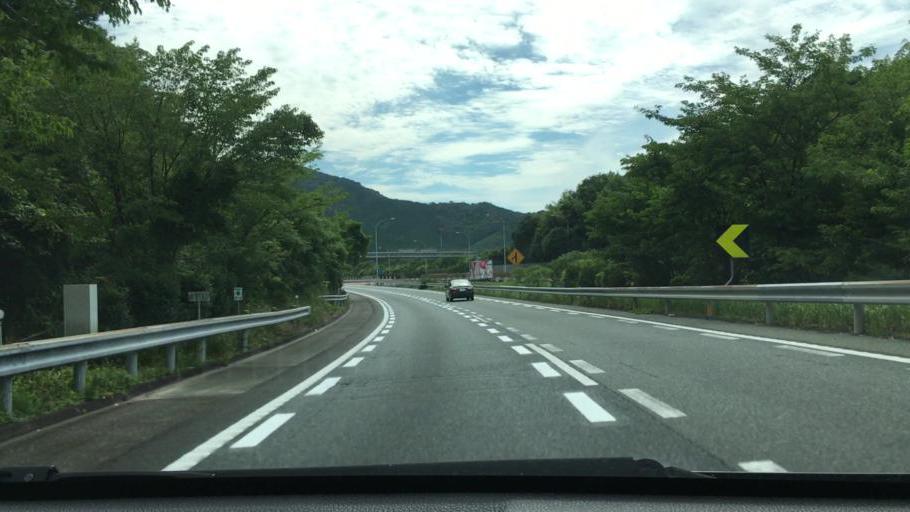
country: JP
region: Yamaguchi
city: Ogori-shimogo
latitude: 34.1322
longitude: 131.4484
